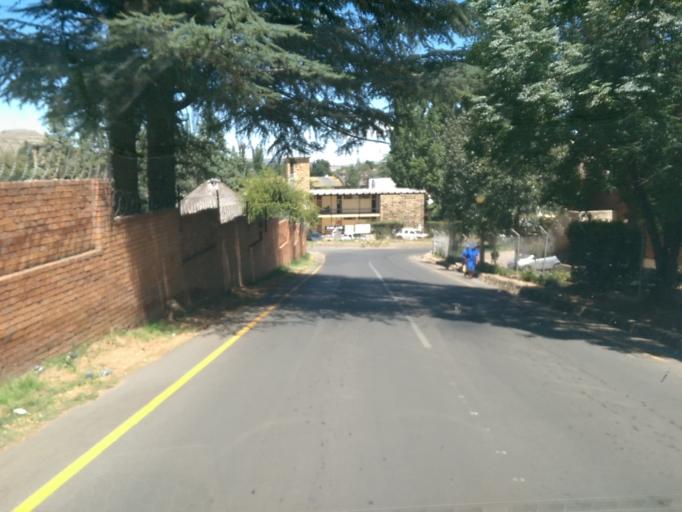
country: LS
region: Maseru
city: Maseru
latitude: -29.3115
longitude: 27.4784
